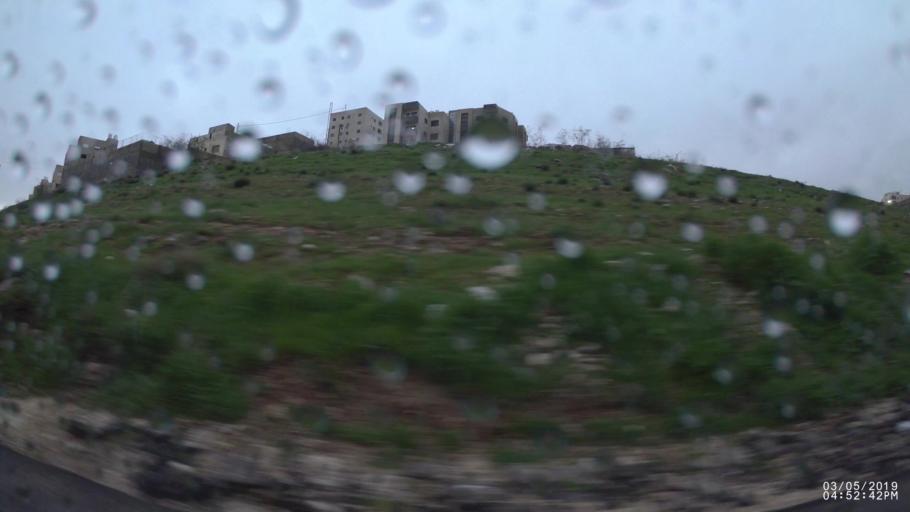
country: JO
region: Amman
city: Amman
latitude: 31.9930
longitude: 35.9725
